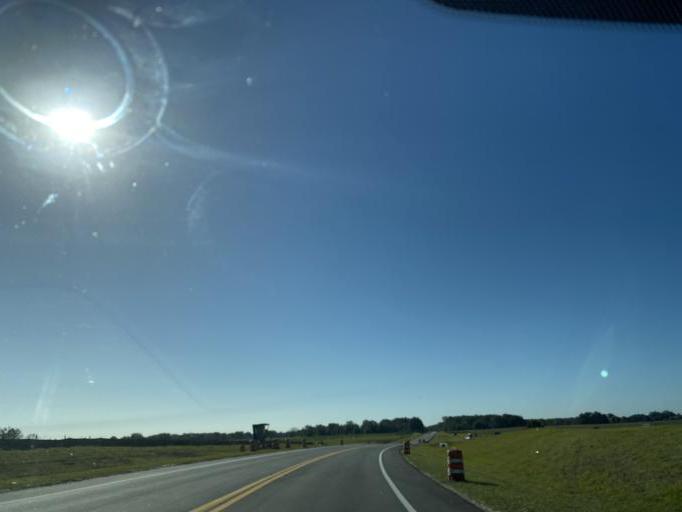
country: US
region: Florida
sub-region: Lake County
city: Mount Plymouth
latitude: 28.8286
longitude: -81.5212
